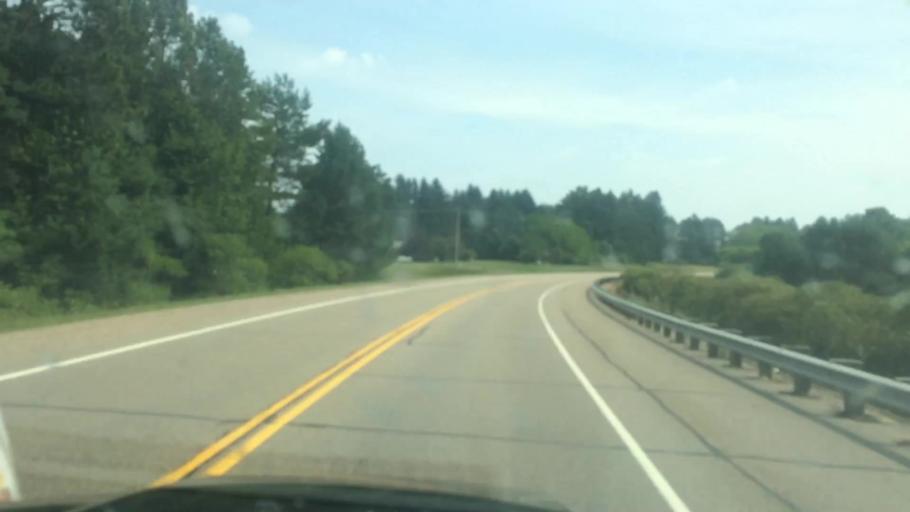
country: US
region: Wisconsin
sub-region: Langlade County
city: Antigo
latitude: 45.1691
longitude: -88.9857
